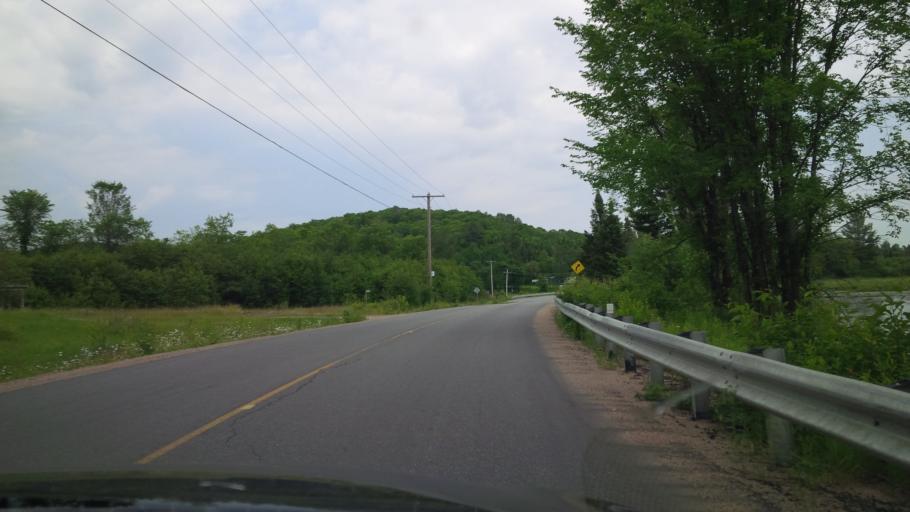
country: CA
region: Ontario
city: Huntsville
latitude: 45.5863
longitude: -79.2170
